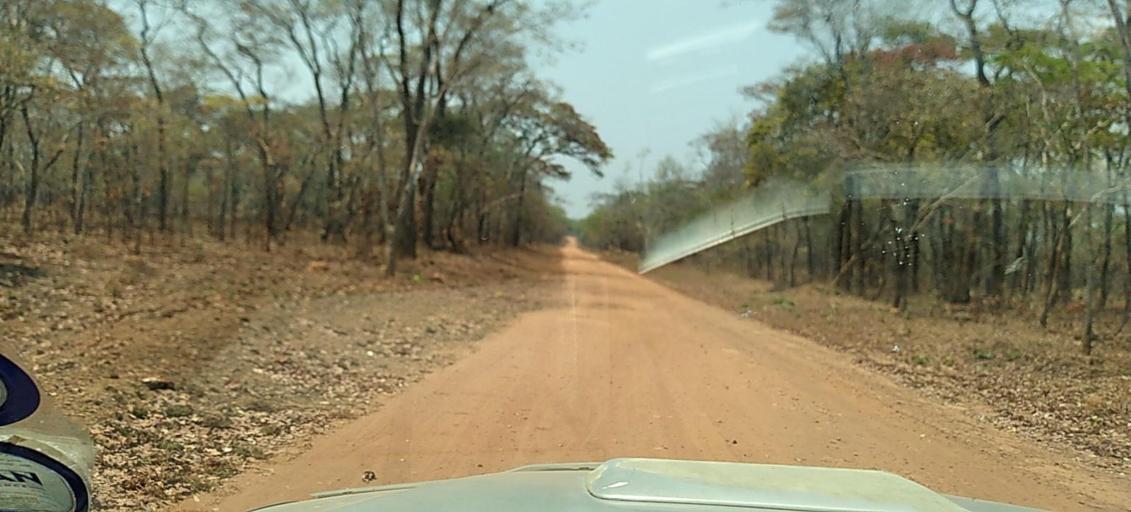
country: ZM
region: North-Western
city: Kasempa
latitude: -13.5586
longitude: 26.0779
